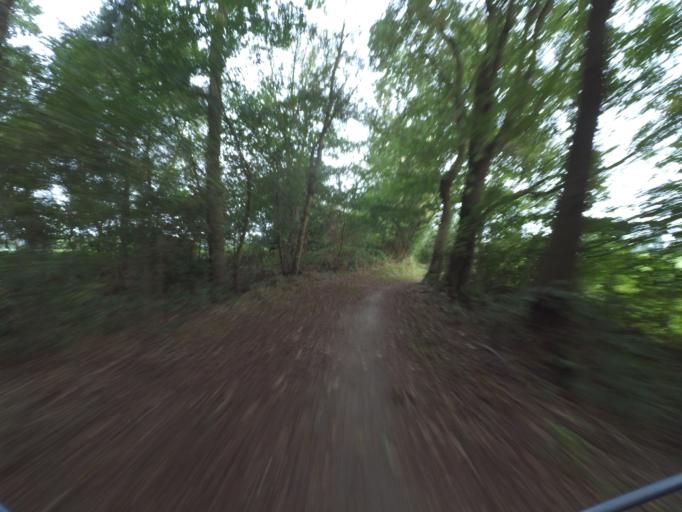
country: DE
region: Lower Saxony
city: Isterberg
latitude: 52.3201
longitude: 7.0859
